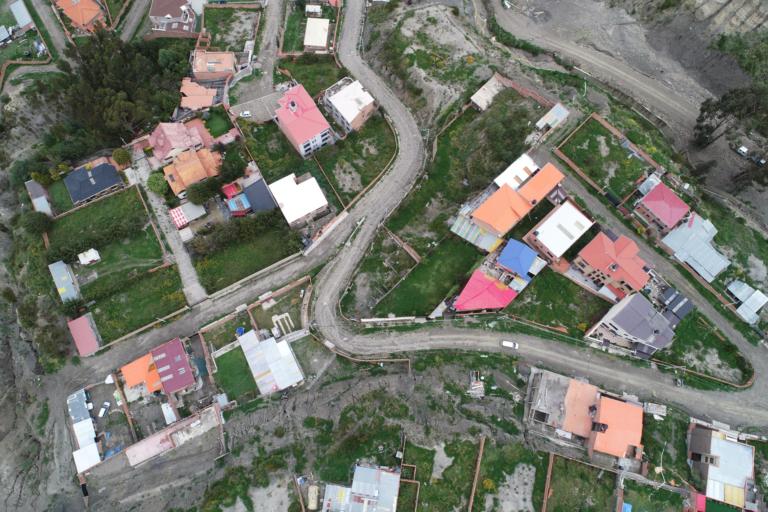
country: BO
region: La Paz
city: La Paz
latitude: -16.4977
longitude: -68.0806
